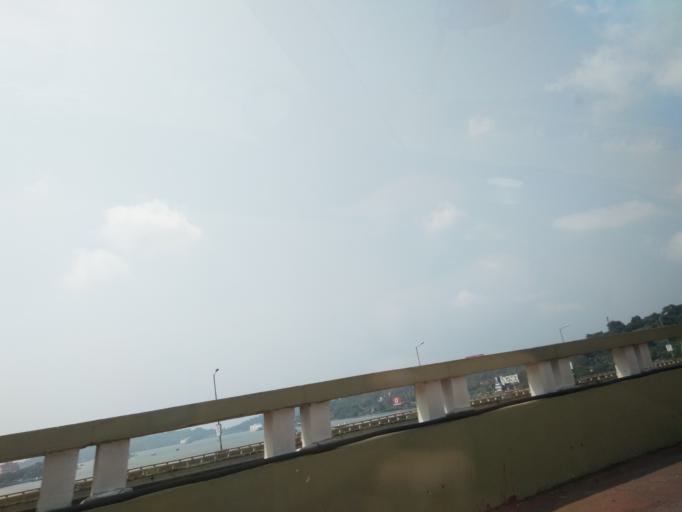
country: IN
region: Goa
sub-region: North Goa
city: Panaji
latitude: 15.5023
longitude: 73.8372
